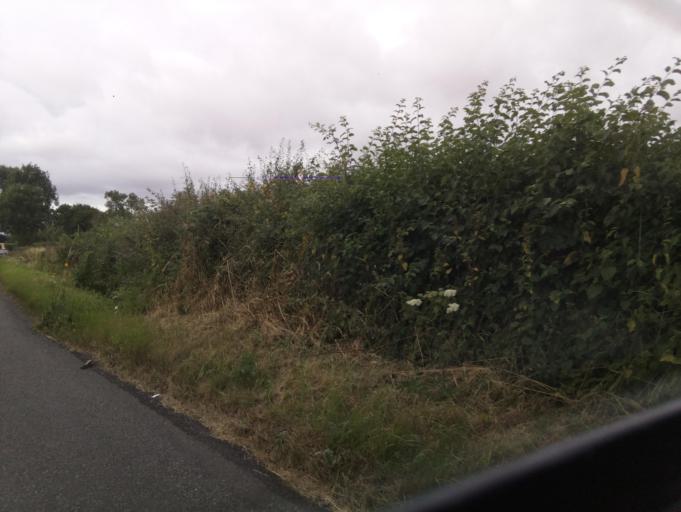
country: GB
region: England
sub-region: Derbyshire
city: Ilkeston
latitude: 52.9263
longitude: -1.3073
